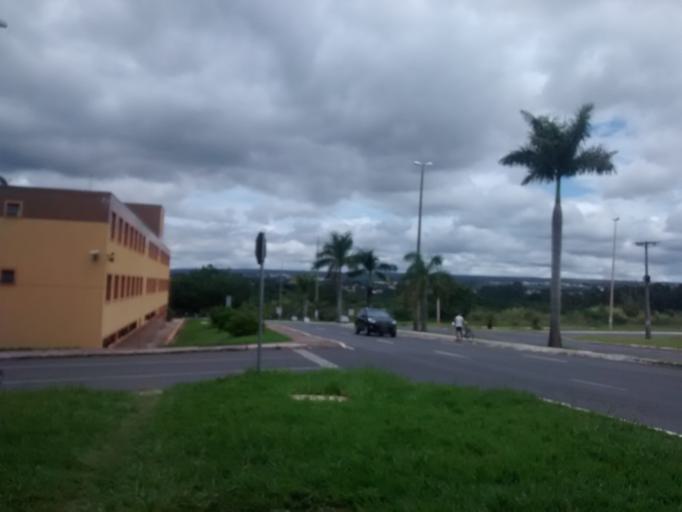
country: BR
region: Federal District
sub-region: Brasilia
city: Brasilia
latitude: -15.7474
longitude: -47.8821
